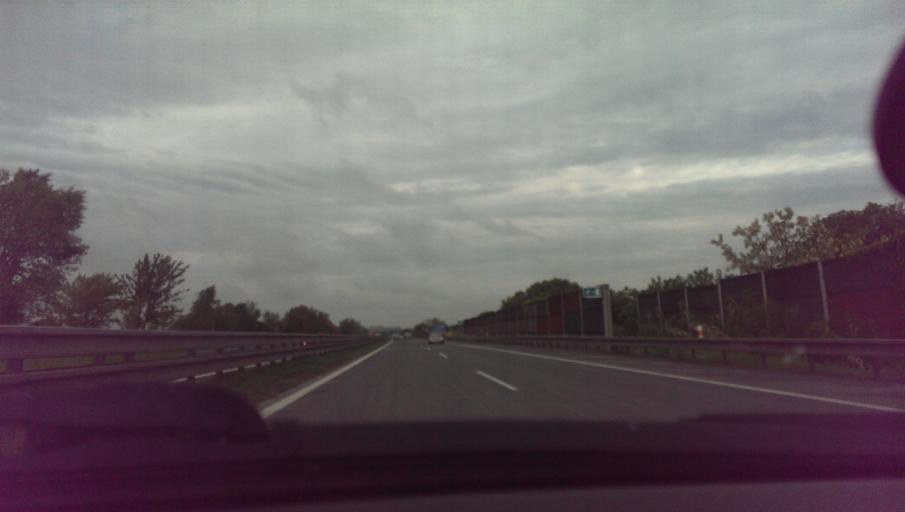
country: CZ
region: South Moravian
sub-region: Okres Vyskov
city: Vyskov
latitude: 49.2659
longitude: 17.0041
